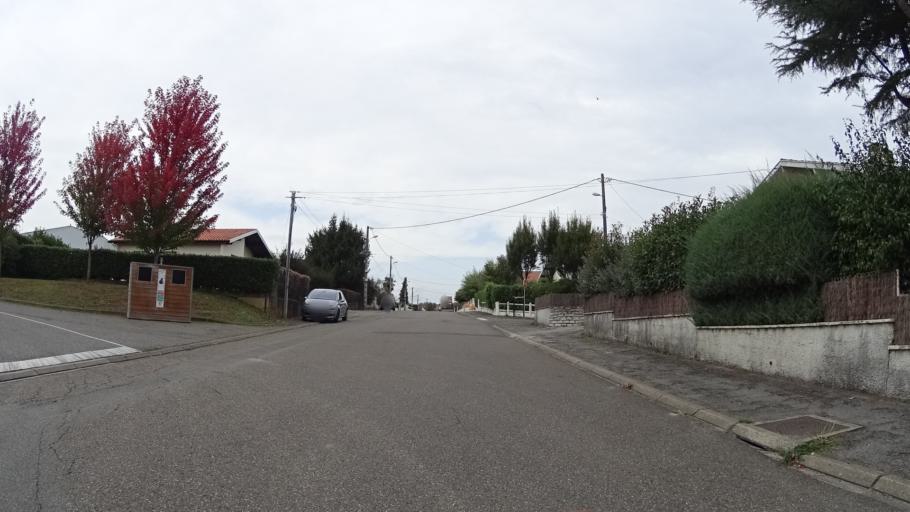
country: FR
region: Aquitaine
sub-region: Departement des Landes
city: Saint-Paul-les-Dax
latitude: 43.7263
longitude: -1.0689
